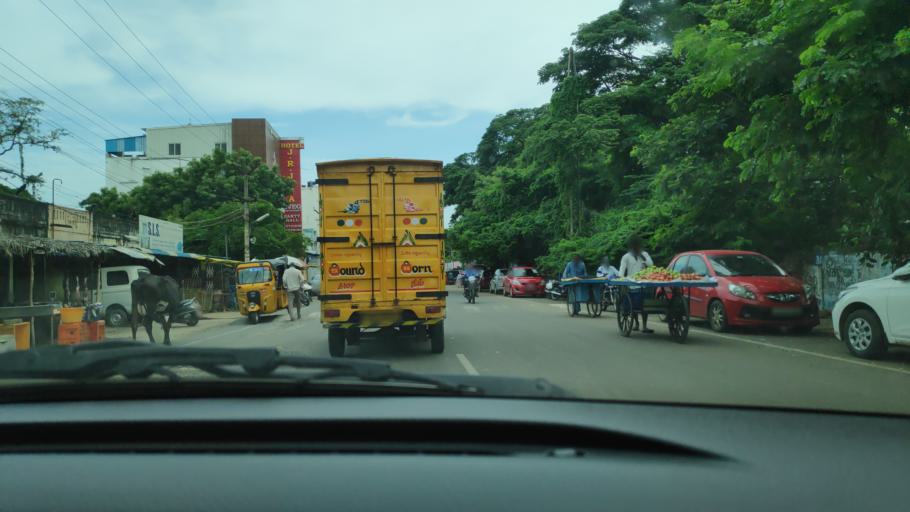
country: IN
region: Tamil Nadu
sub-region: Kancheepuram
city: Vengavasal
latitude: 12.9242
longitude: 80.1260
